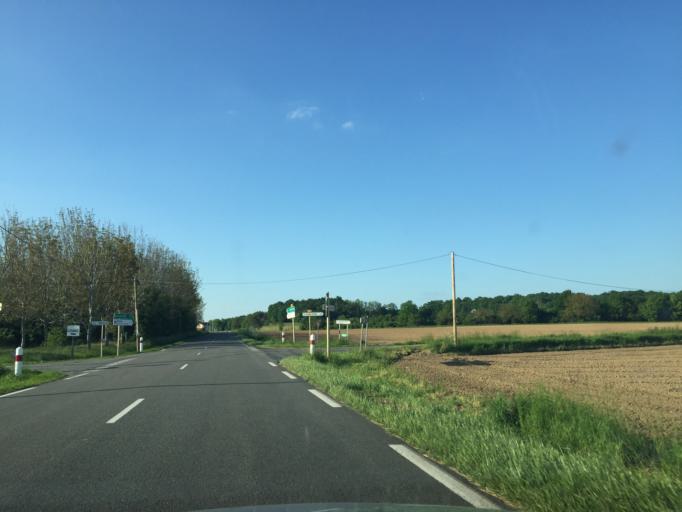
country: FR
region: Poitou-Charentes
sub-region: Departement de la Charente
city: Chalais
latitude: 45.2184
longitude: 0.0338
